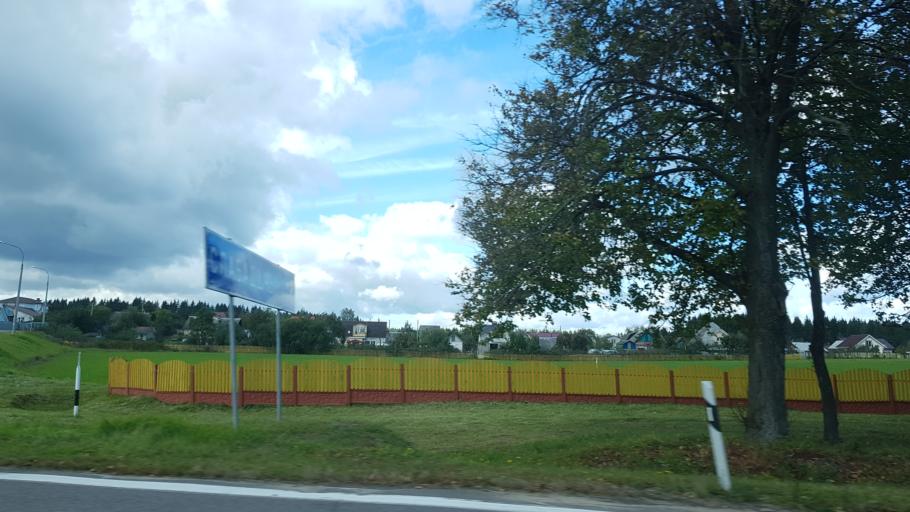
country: BY
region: Minsk
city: Korolev Stan
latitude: 53.9981
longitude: 27.8242
